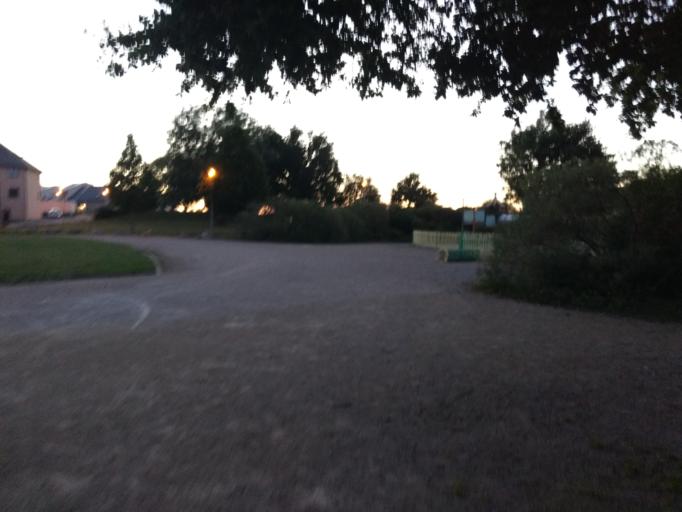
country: FR
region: Midi-Pyrenees
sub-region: Departement de l'Aveyron
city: Olemps
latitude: 44.3386
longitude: 2.5543
